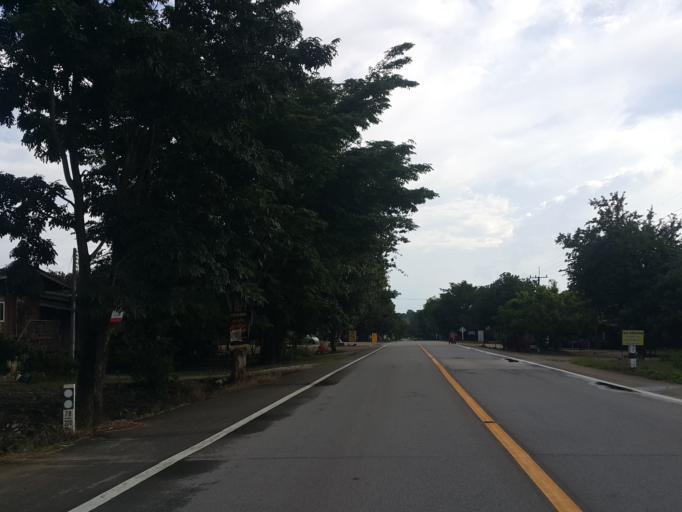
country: TH
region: Chiang Mai
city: Phrao
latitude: 19.2392
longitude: 99.1861
